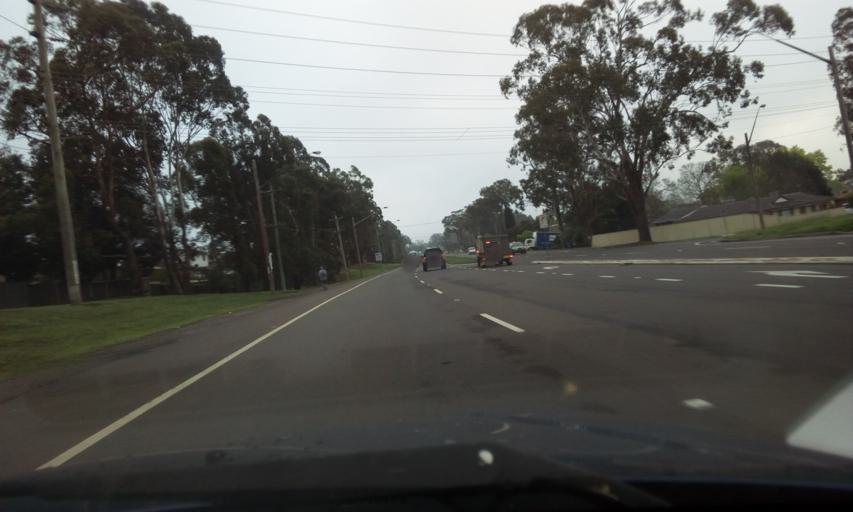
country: AU
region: New South Wales
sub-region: Camden
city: Camden South
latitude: -34.0829
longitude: 150.6947
